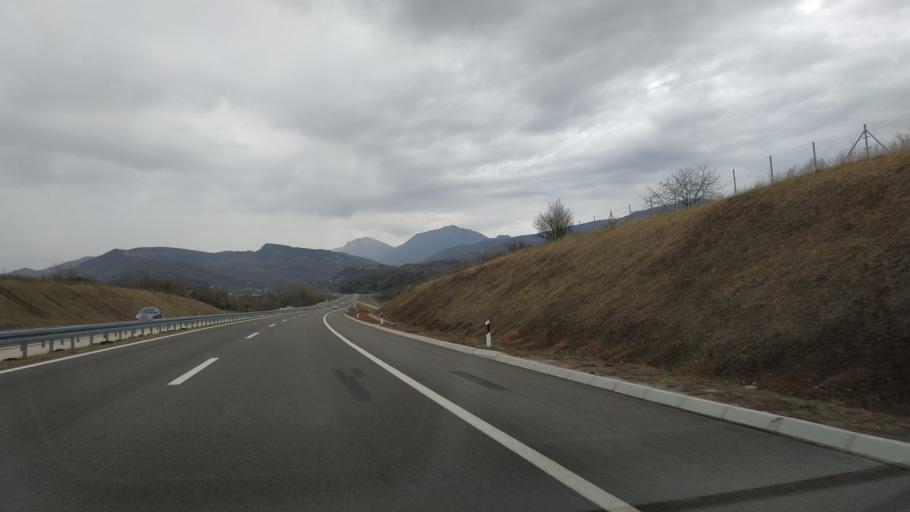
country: RS
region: Central Serbia
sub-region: Nisavski Okrug
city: Niska Banja
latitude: 43.3113
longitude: 22.0336
